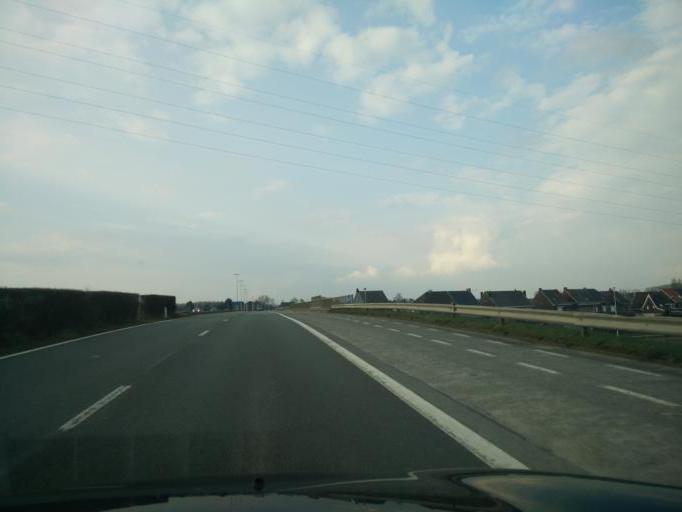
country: BE
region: Flanders
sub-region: Provincie Oost-Vlaanderen
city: Perre
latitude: 50.8823
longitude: 3.8351
